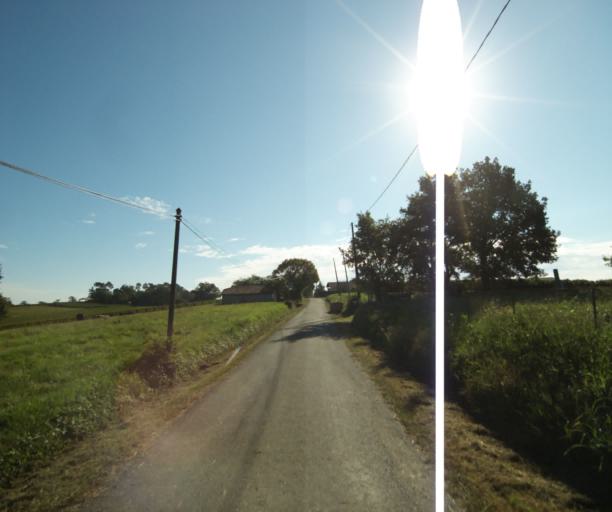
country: FR
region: Aquitaine
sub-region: Departement des Landes
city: Gabarret
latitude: 43.9065
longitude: 0.0163
